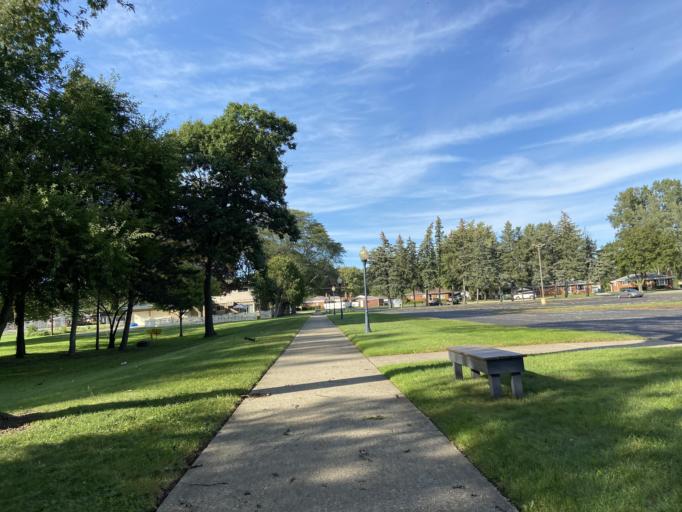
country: US
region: Michigan
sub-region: Oakland County
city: Farmington
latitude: 42.4499
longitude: -83.3229
